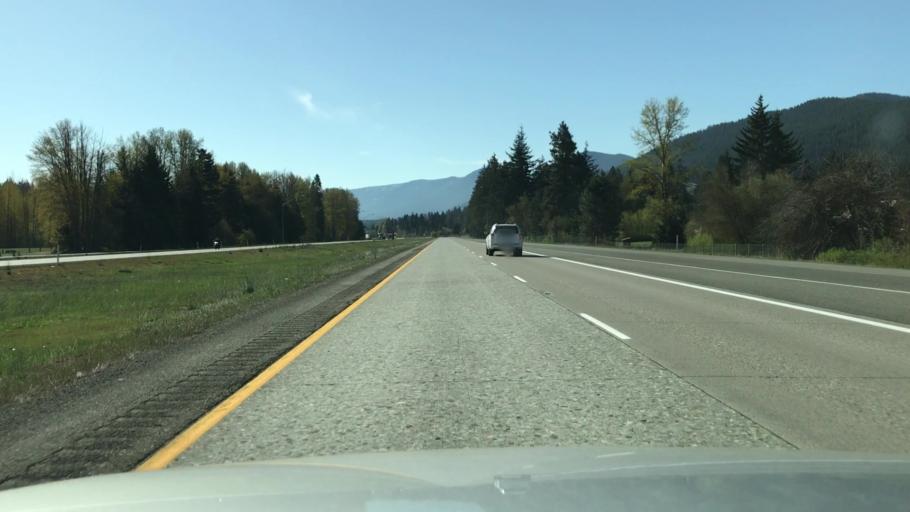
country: US
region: Washington
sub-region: Kittitas County
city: Cle Elum
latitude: 47.2338
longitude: -121.1708
